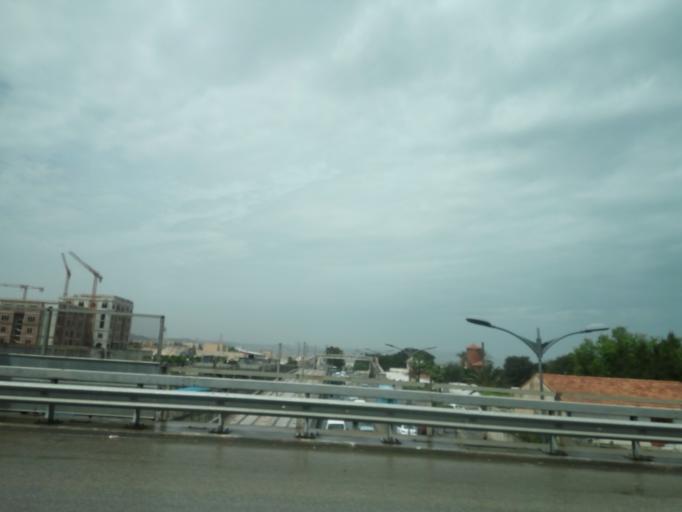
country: DZ
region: Alger
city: Bab Ezzouar
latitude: 36.7353
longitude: 3.1206
